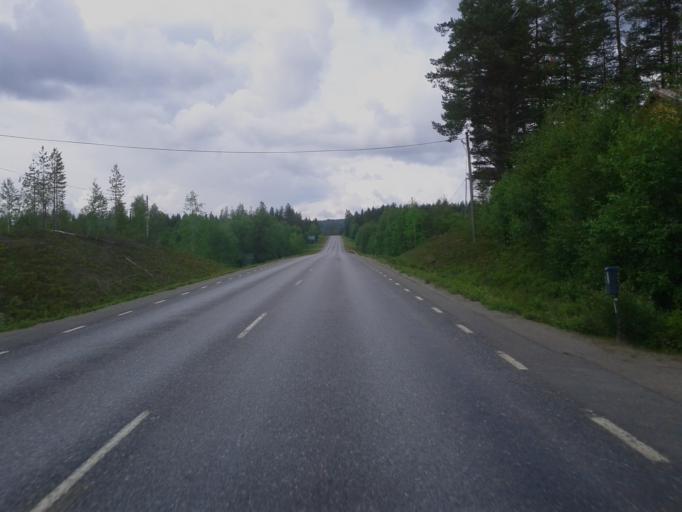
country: SE
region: Vaesterbotten
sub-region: Norsjo Kommun
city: Norsjoe
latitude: 64.9879
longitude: 19.4333
